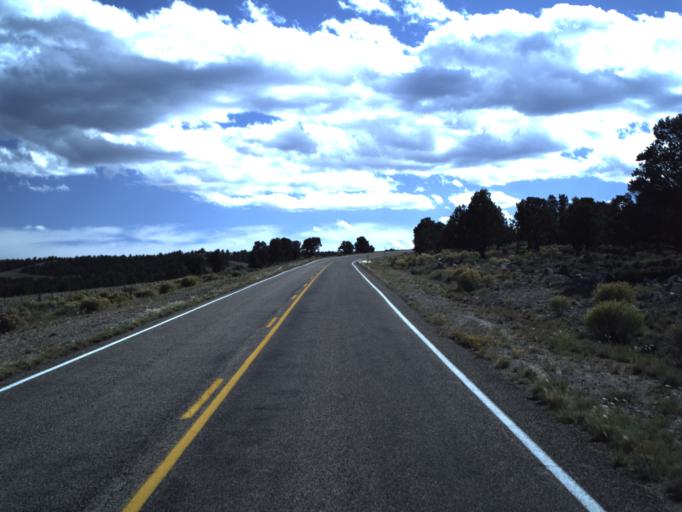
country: US
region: Utah
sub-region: Garfield County
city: Panguitch
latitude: 37.7943
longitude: -112.4370
